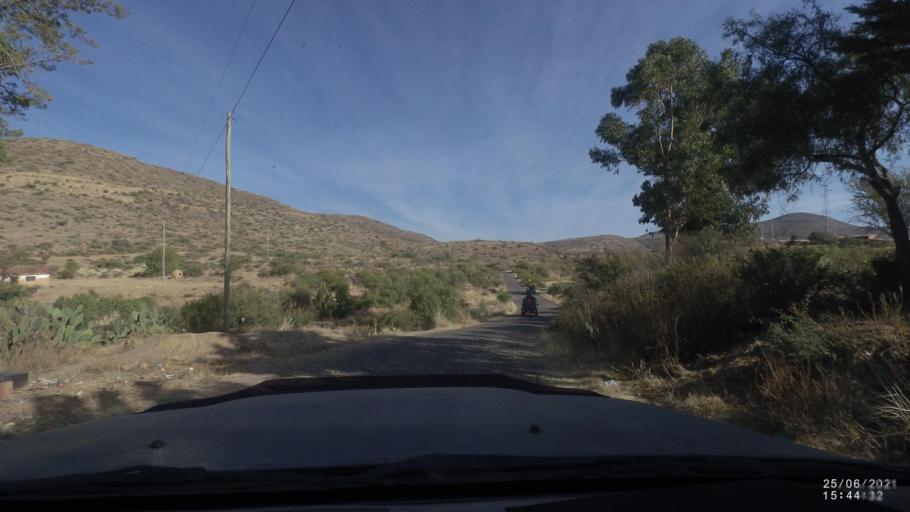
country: BO
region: Cochabamba
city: Cliza
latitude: -17.6572
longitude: -65.9107
